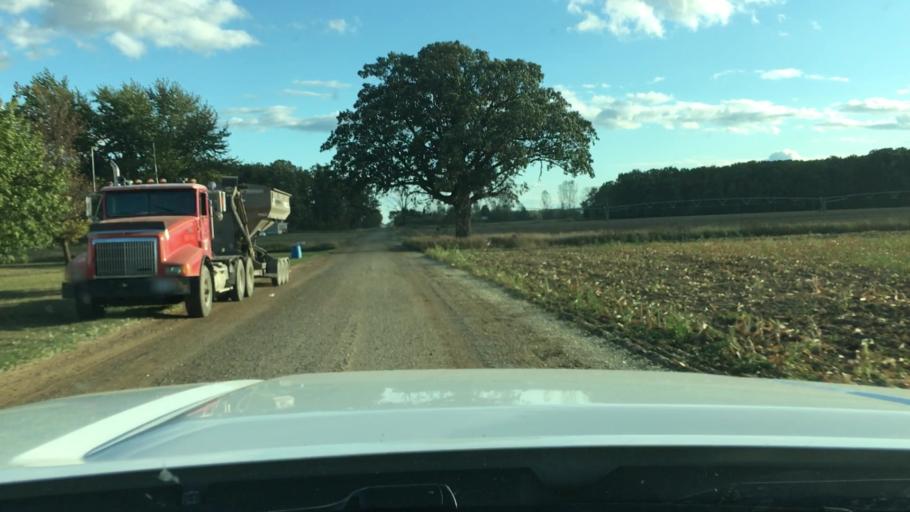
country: US
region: Michigan
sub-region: Clinton County
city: Saint Johns
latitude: 43.0925
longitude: -84.4839
